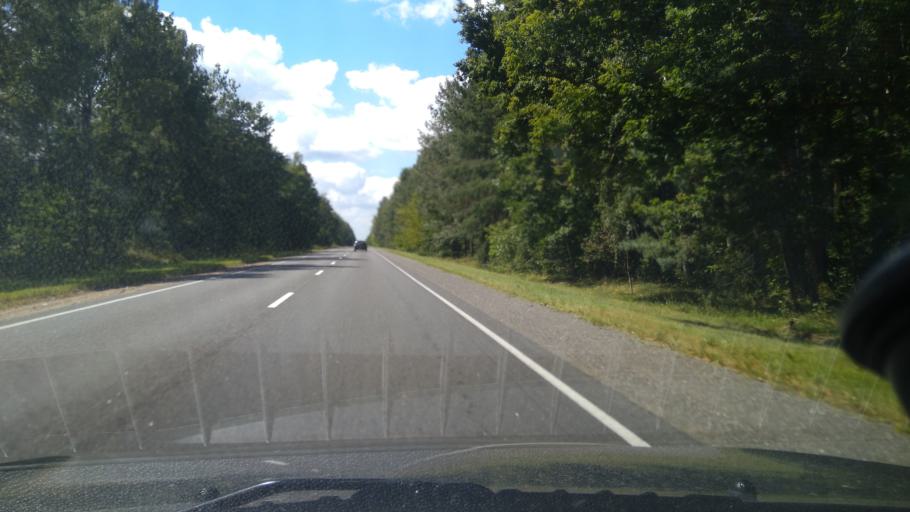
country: BY
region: Brest
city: Nyakhachava
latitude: 52.6637
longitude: 25.2455
